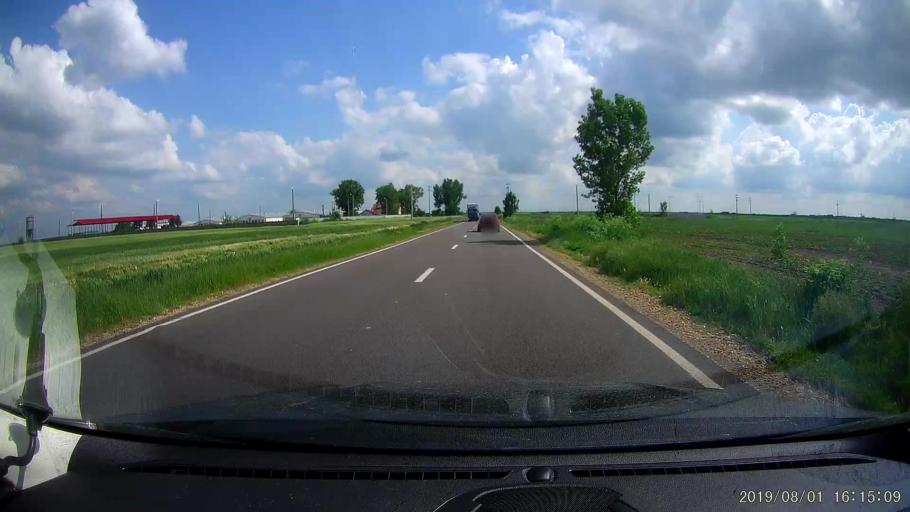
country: RO
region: Calarasi
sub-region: Comuna Stefan Voda
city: Stefan Voda
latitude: 44.3427
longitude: 27.3619
